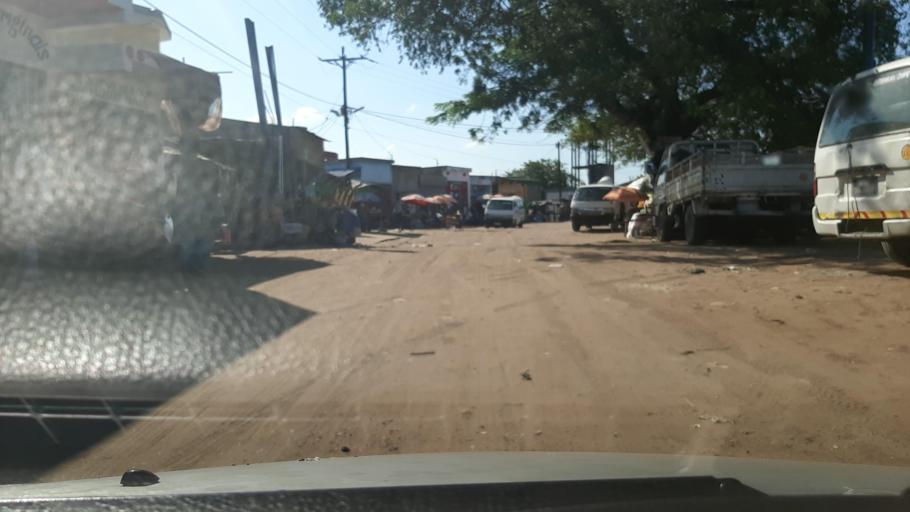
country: MZ
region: Maputo
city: Matola
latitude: -25.7924
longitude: 32.4882
